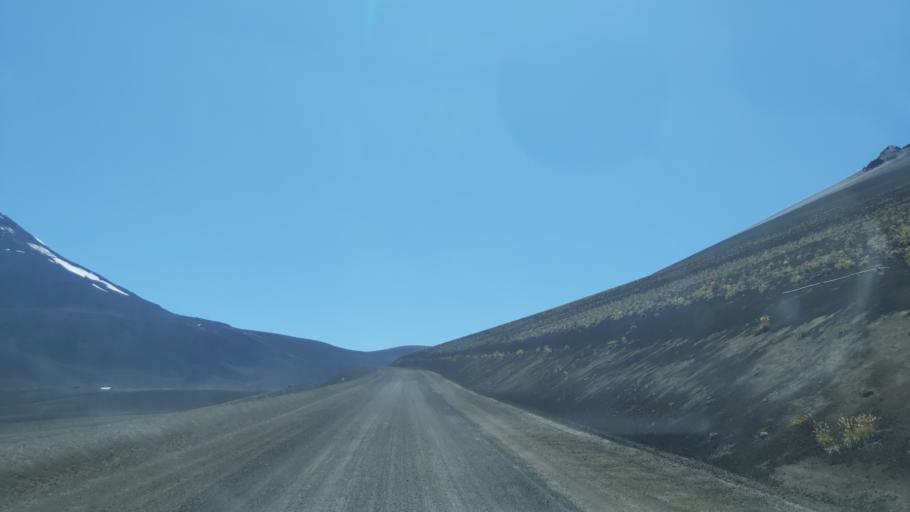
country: CL
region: Araucania
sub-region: Provincia de Cautin
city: Vilcun
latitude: -38.4073
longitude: -71.5425
